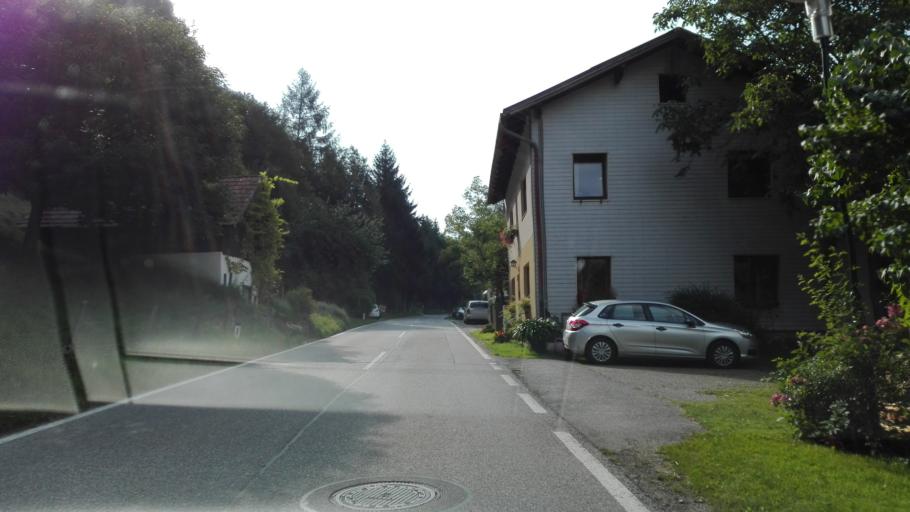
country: AT
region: Lower Austria
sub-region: Politischer Bezirk Sankt Polten
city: Stossing
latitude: 48.0949
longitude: 15.7711
